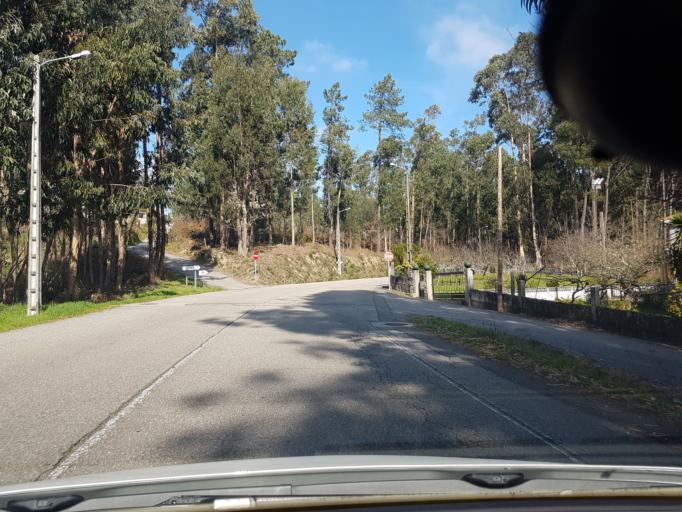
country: ES
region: Galicia
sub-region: Provincia de Pontevedra
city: Porrino
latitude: 42.2051
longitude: -8.6446
